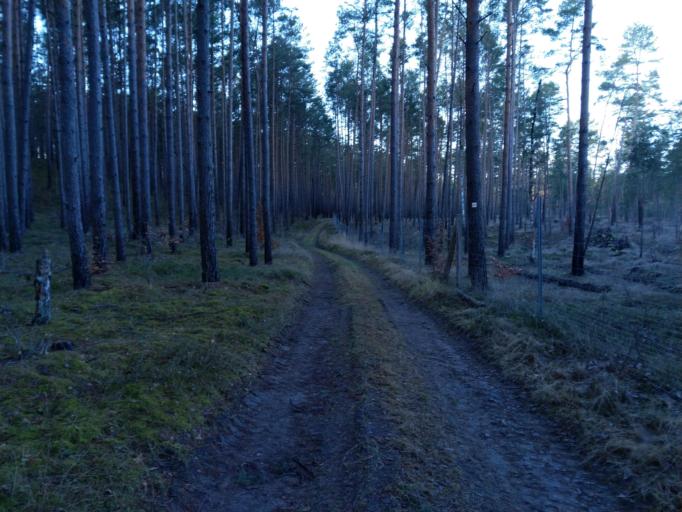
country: DE
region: Brandenburg
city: Biesenthal
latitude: 52.7803
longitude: 13.5941
